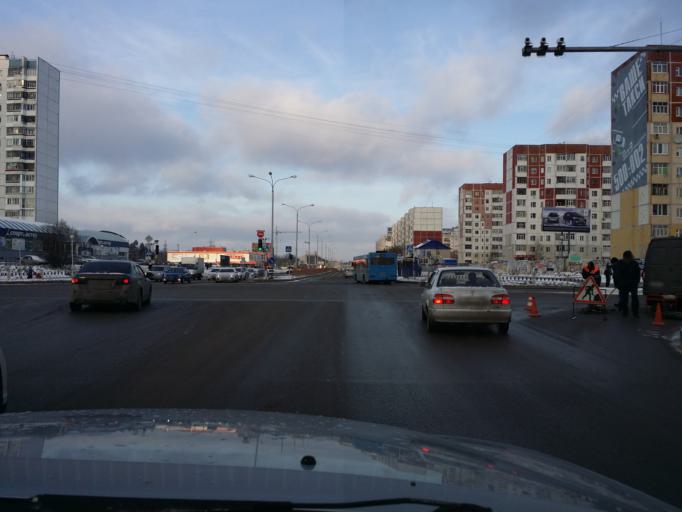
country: RU
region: Khanty-Mansiyskiy Avtonomnyy Okrug
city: Nizhnevartovsk
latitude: 60.9447
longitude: 76.6014
